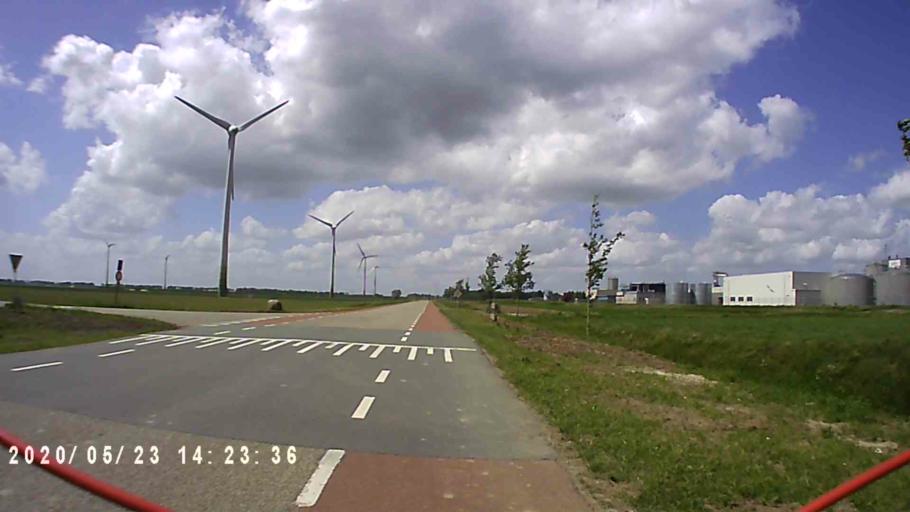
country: NL
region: Groningen
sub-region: Gemeente Delfzijl
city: Delfzijl
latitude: 53.2909
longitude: 6.9777
